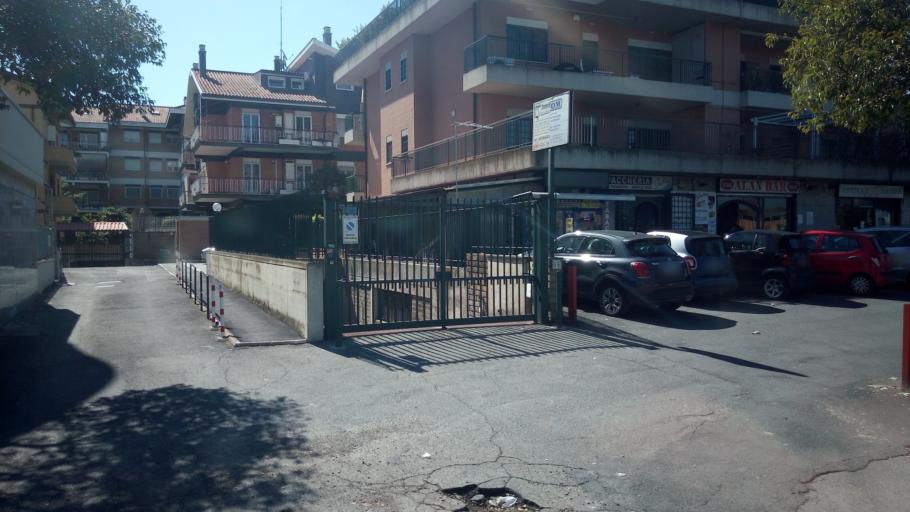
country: IT
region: Latium
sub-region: Citta metropolitana di Roma Capitale
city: Ciampino
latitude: 41.8194
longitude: 12.6110
